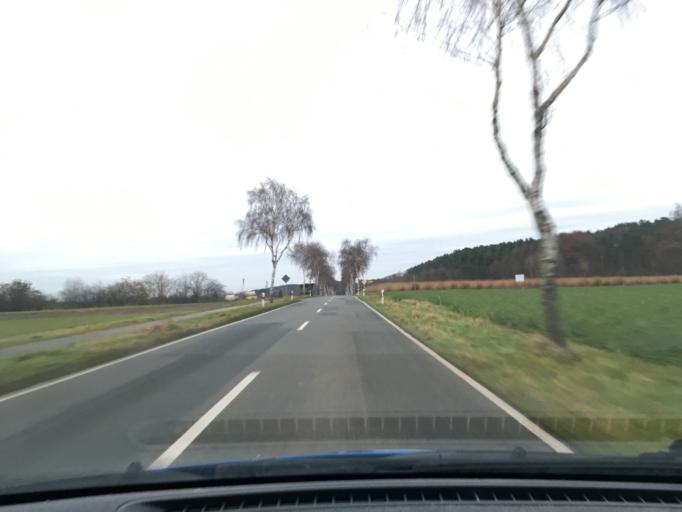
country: DE
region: Lower Saxony
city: Neu Darchau
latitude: 53.2360
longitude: 10.8594
